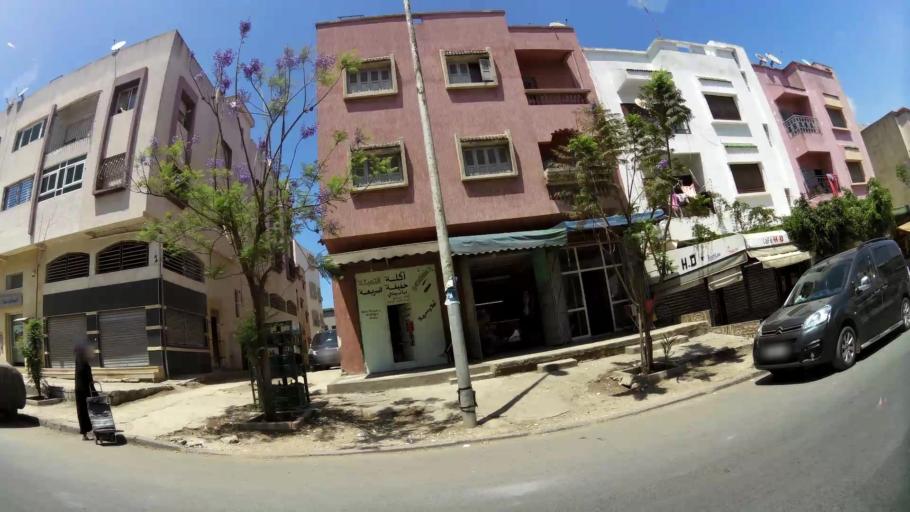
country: MA
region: Gharb-Chrarda-Beni Hssen
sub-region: Kenitra Province
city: Kenitra
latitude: 34.2596
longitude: -6.5563
